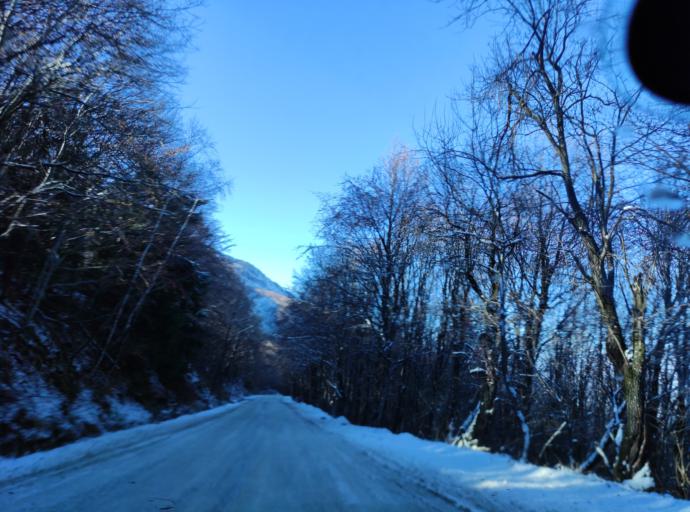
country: BG
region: Sofia-Capital
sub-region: Stolichna Obshtina
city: Sofia
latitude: 42.6062
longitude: 23.3069
